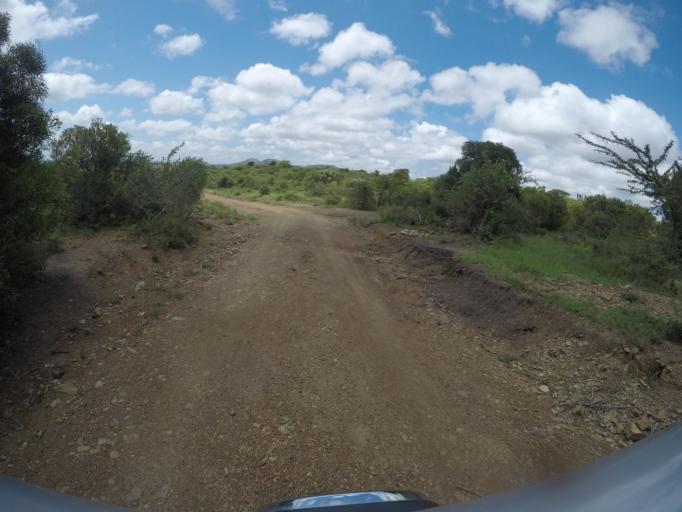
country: ZA
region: KwaZulu-Natal
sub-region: uThungulu District Municipality
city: Empangeni
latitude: -28.5851
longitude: 31.8289
